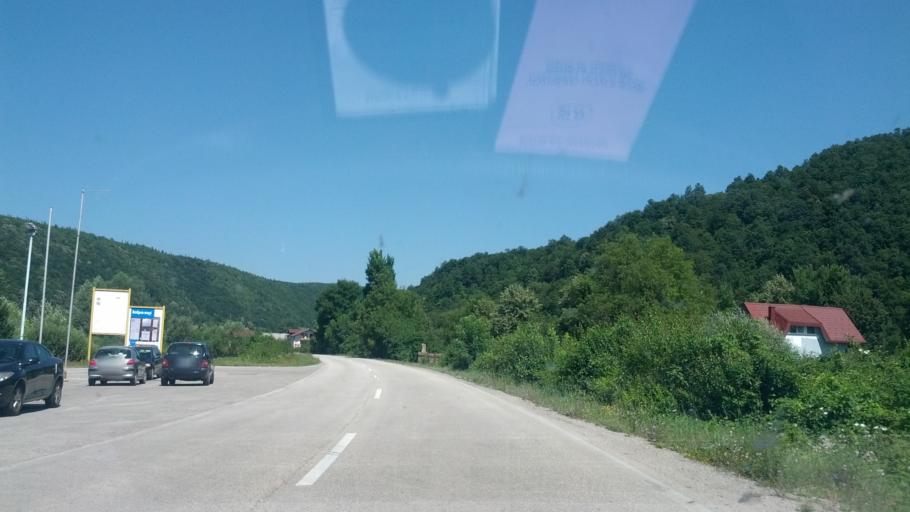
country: BA
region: Federation of Bosnia and Herzegovina
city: Bosanska Krupa
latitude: 44.9120
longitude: 16.1570
